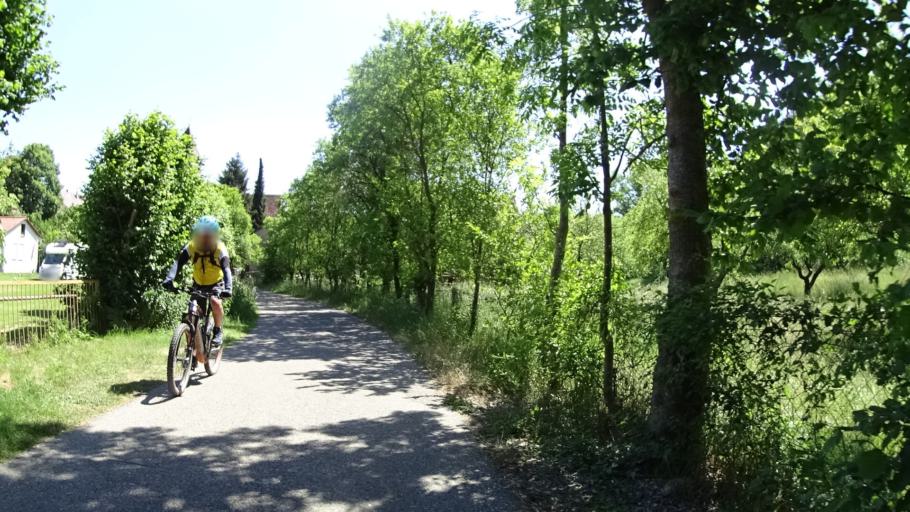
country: DE
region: Bavaria
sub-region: Regierungsbezirk Mittelfranken
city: Rothenburg ob der Tauber
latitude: 49.3881
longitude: 10.1660
